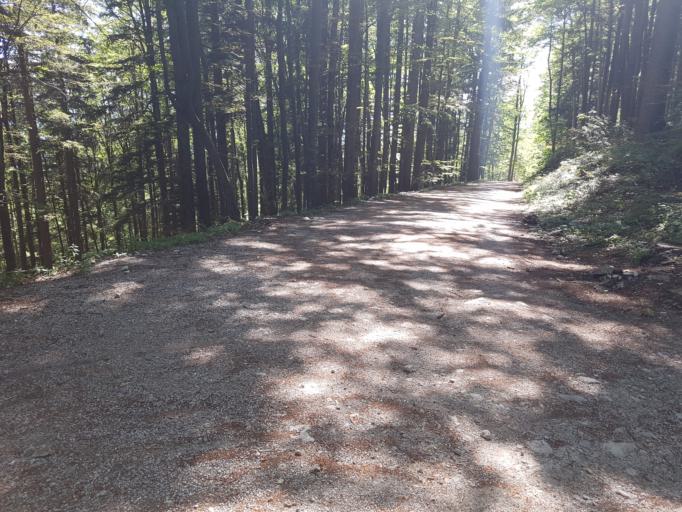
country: AT
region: Salzburg
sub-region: Politischer Bezirk Salzburg-Umgebung
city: Koppl
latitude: 47.8016
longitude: 13.1284
